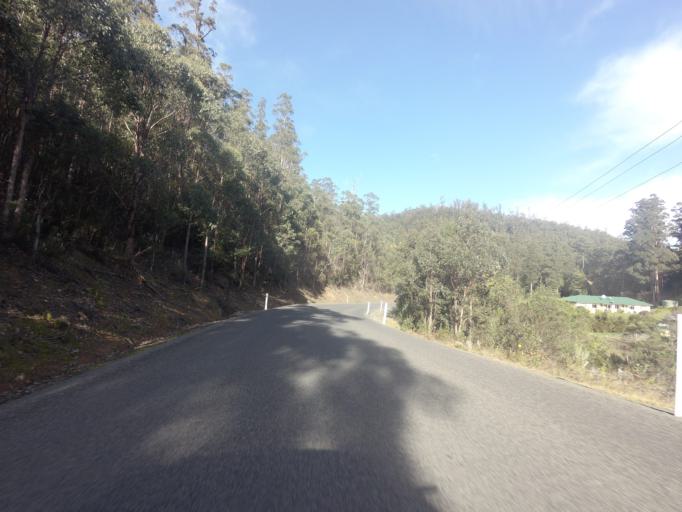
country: AU
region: Tasmania
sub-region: Huon Valley
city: Huonville
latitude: -43.0400
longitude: 147.1334
